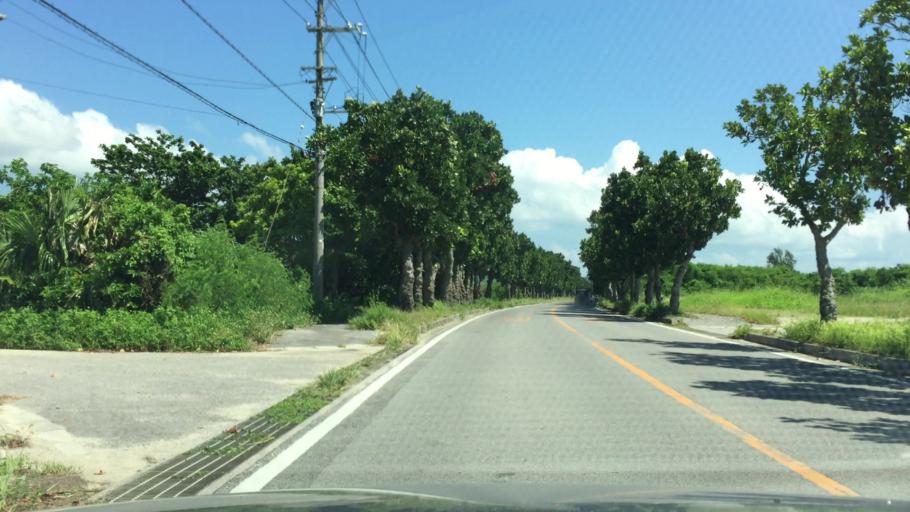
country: JP
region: Okinawa
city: Ishigaki
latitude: 24.3652
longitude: 124.2465
